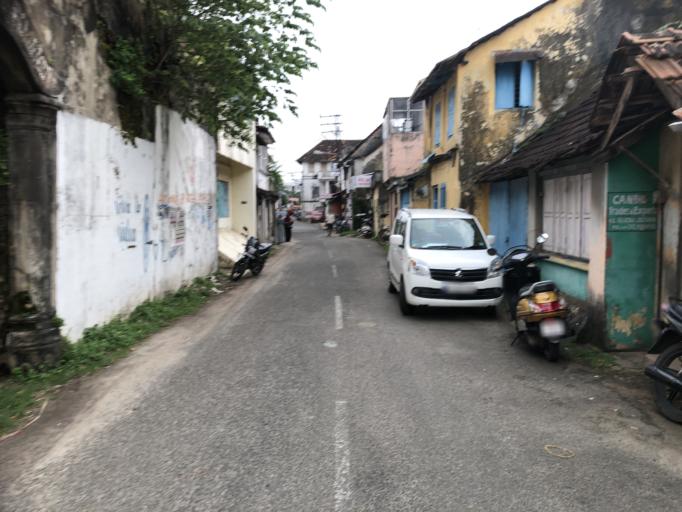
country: IN
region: Kerala
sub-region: Ernakulam
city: Cochin
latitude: 9.9547
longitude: 76.2603
